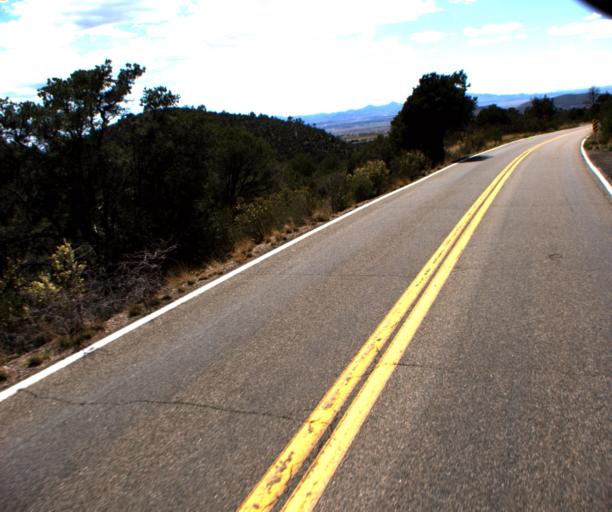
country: US
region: Arizona
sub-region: Yavapai County
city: Prescott Valley
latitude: 34.6779
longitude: -112.1867
